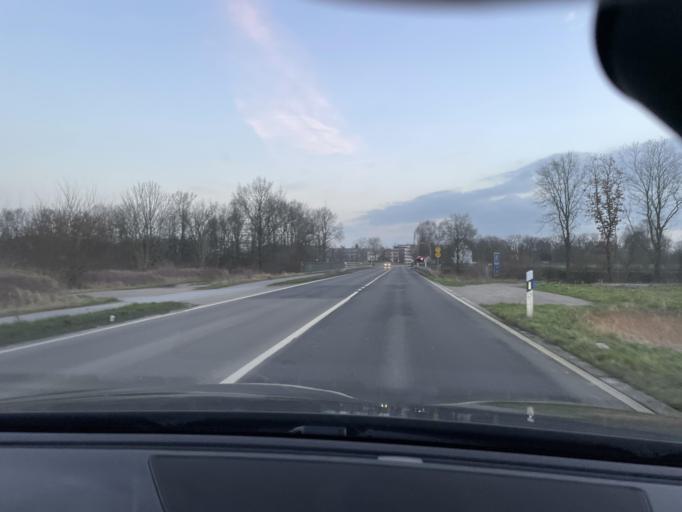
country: DE
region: North Rhine-Westphalia
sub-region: Regierungsbezirk Dusseldorf
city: Viersen
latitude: 51.2232
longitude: 6.4154
